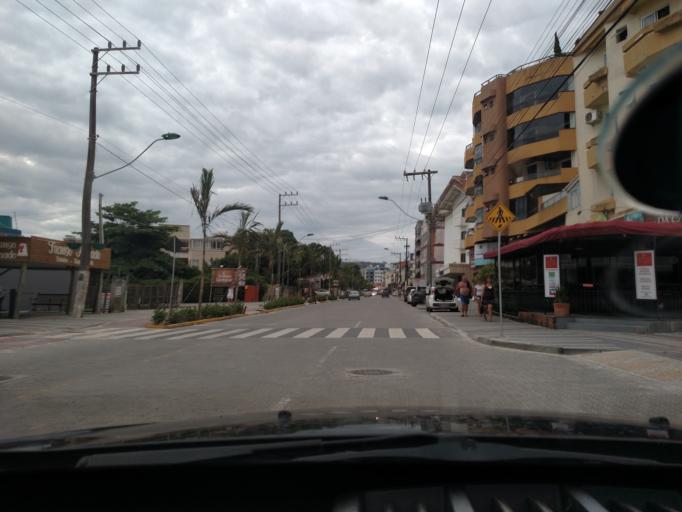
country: BR
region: Santa Catarina
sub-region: Porto Belo
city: Porto Belo
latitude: -27.1393
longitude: -48.5100
